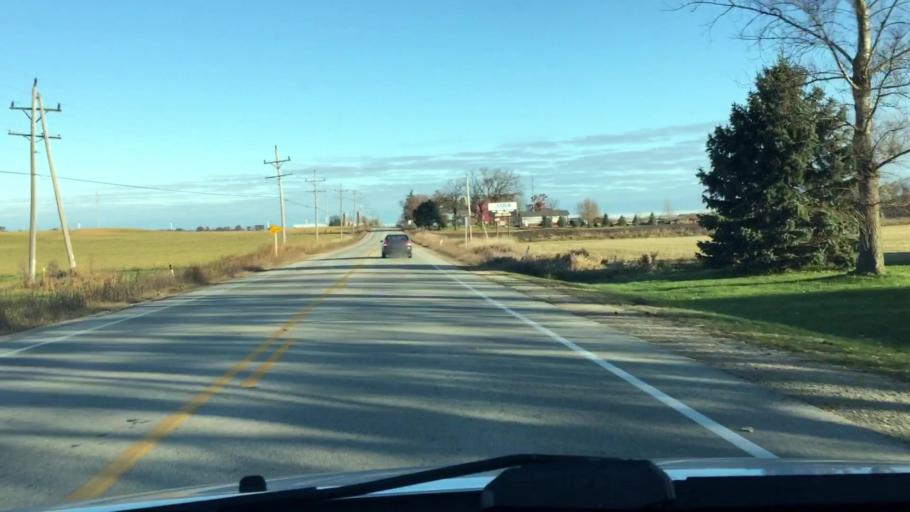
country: US
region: Wisconsin
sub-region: Dodge County
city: Lomira
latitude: 43.6048
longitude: -88.4503
